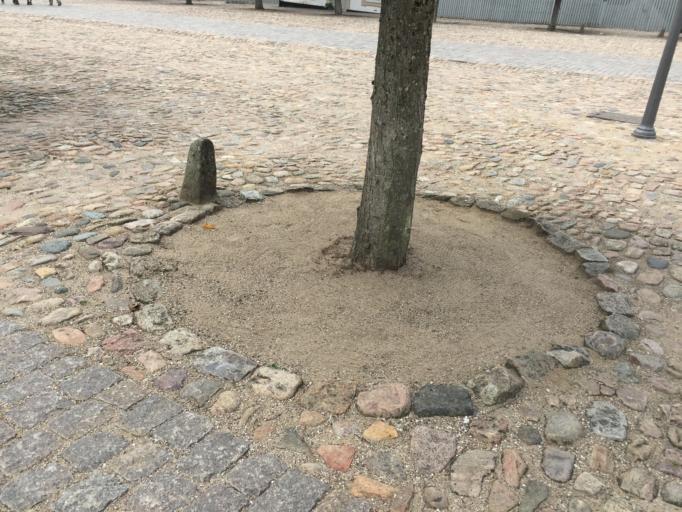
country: DK
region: Capital Region
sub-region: Fredensborg Kommune
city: Fredensborg
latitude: 55.9811
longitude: 12.3962
